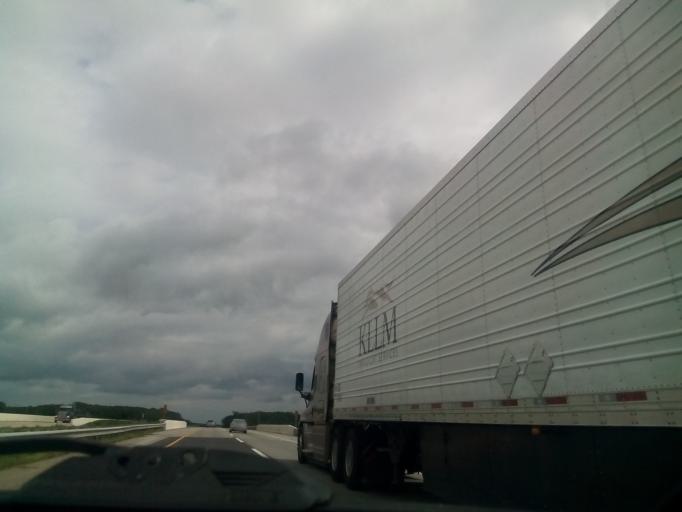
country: US
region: Indiana
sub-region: Steuben County
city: Fremont
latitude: 41.7130
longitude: -84.9462
